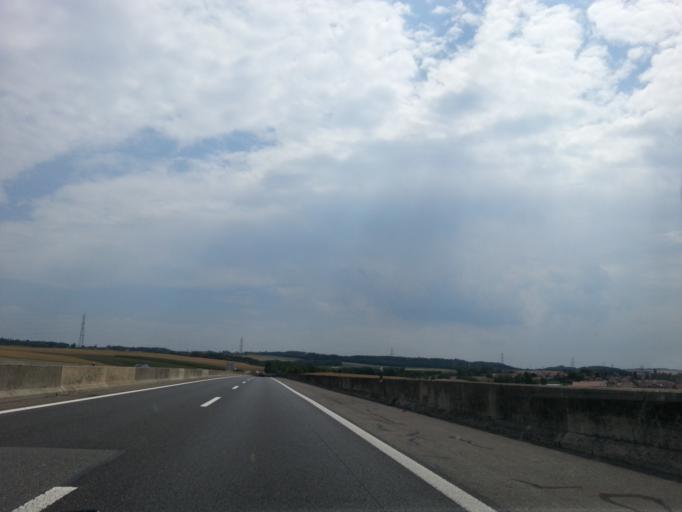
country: CH
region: Vaud
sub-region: Jura-Nord vaudois District
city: Chavornay
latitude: 46.7206
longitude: 6.5721
